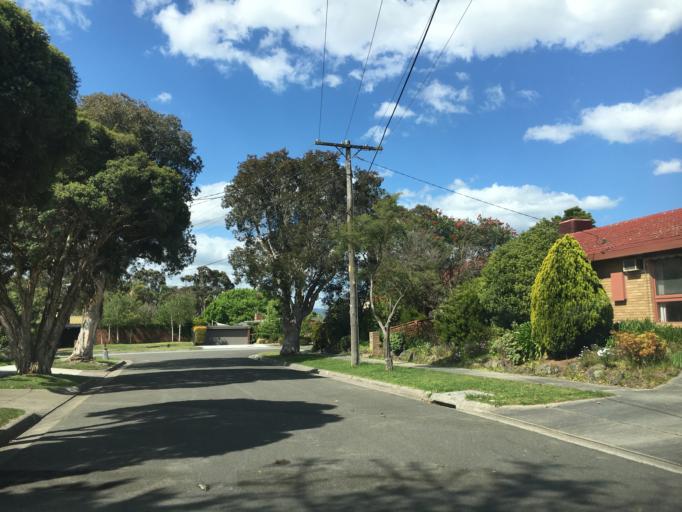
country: AU
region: Victoria
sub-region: Monash
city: Mulgrave
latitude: -37.8930
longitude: 145.1866
